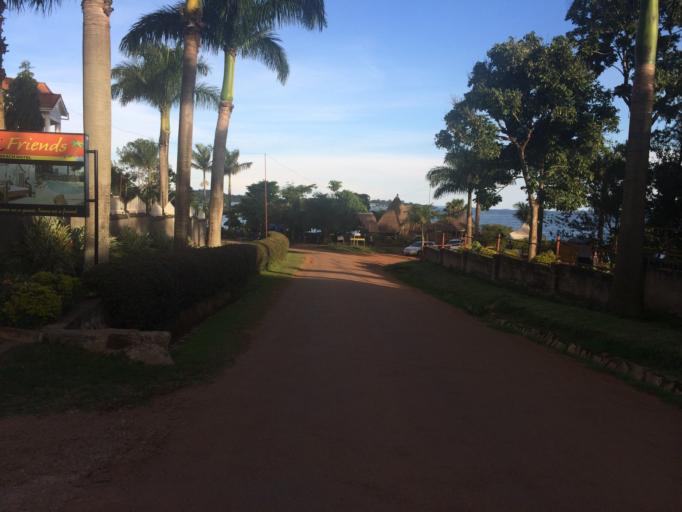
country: UG
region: Central Region
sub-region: Wakiso District
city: Entebbe
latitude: 0.0701
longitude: 32.4804
